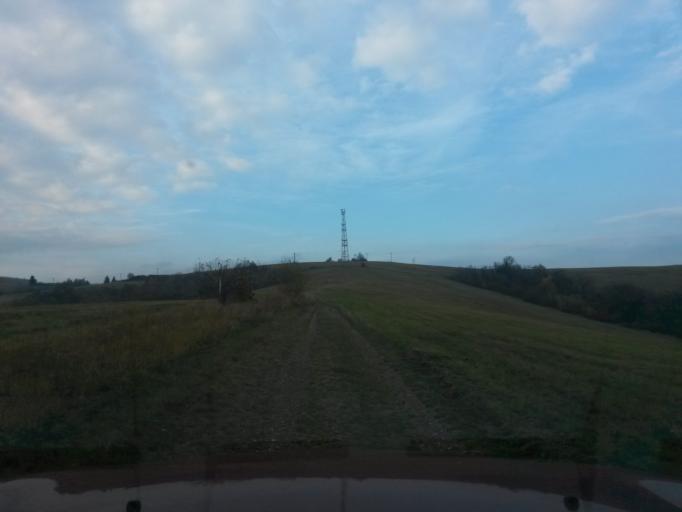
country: SK
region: Kosicky
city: Kosice
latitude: 48.7640
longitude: 21.2108
